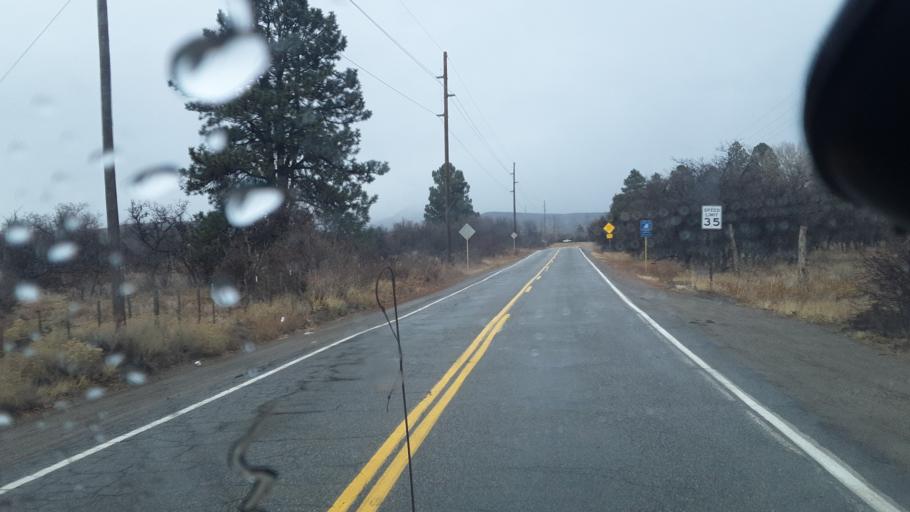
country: US
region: Colorado
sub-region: La Plata County
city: Durango
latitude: 37.2506
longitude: -108.0359
